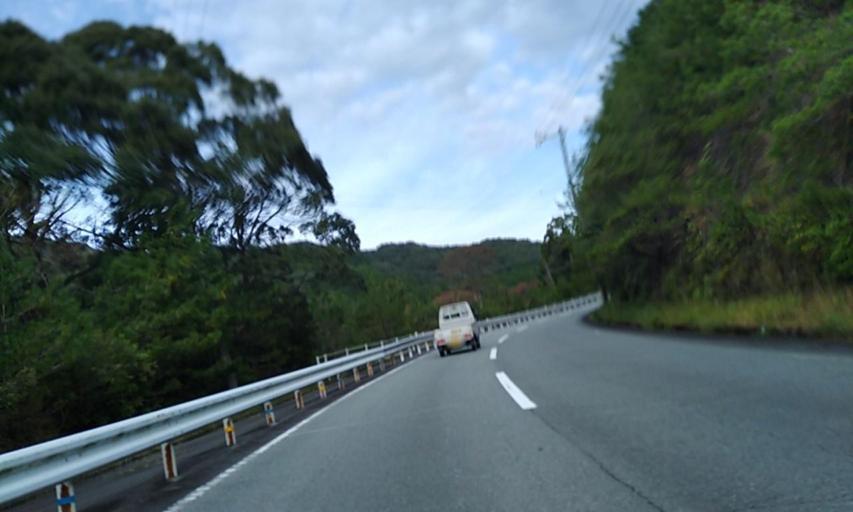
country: JP
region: Mie
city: Ise
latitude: 34.3007
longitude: 136.6046
